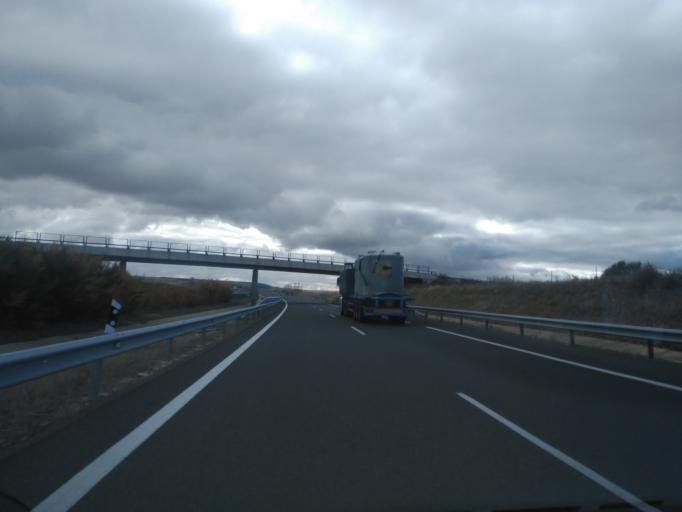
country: ES
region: Castille and Leon
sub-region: Provincia de Palencia
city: Pina de Campos
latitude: 42.2093
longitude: -4.4478
